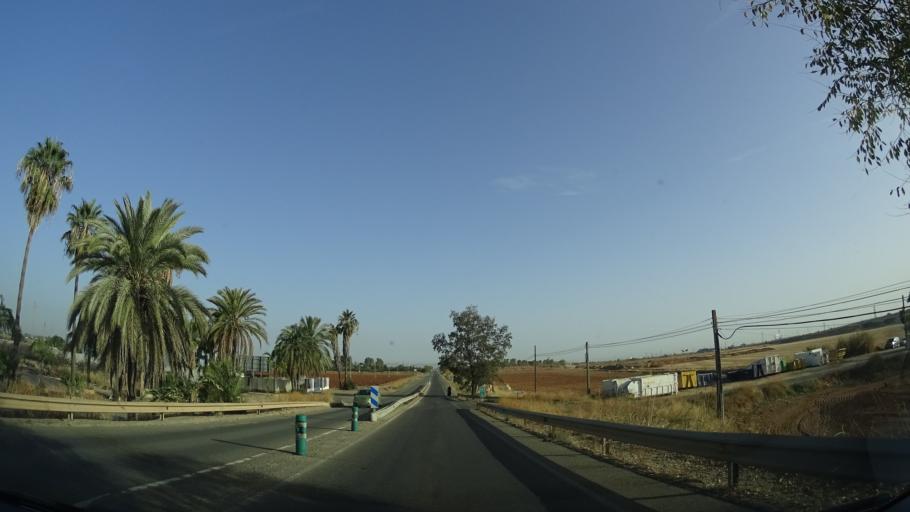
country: ES
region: Andalusia
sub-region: Provincia de Sevilla
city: La Algaba
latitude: 37.4355
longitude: -5.9793
